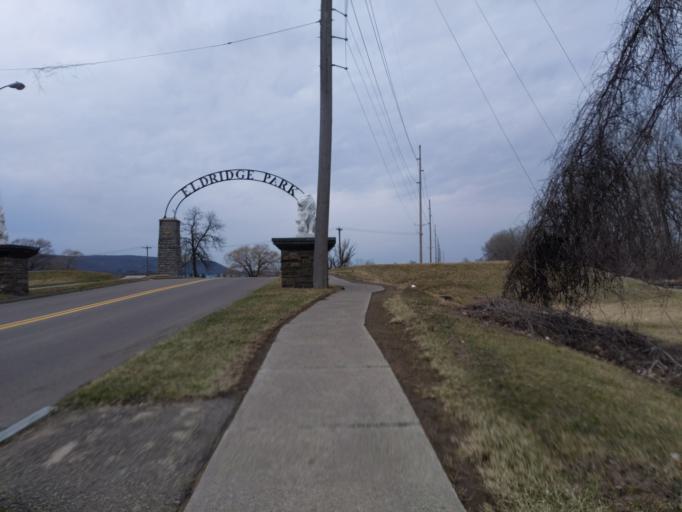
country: US
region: New York
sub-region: Chemung County
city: Elmira Heights
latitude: 42.1119
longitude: -76.8147
